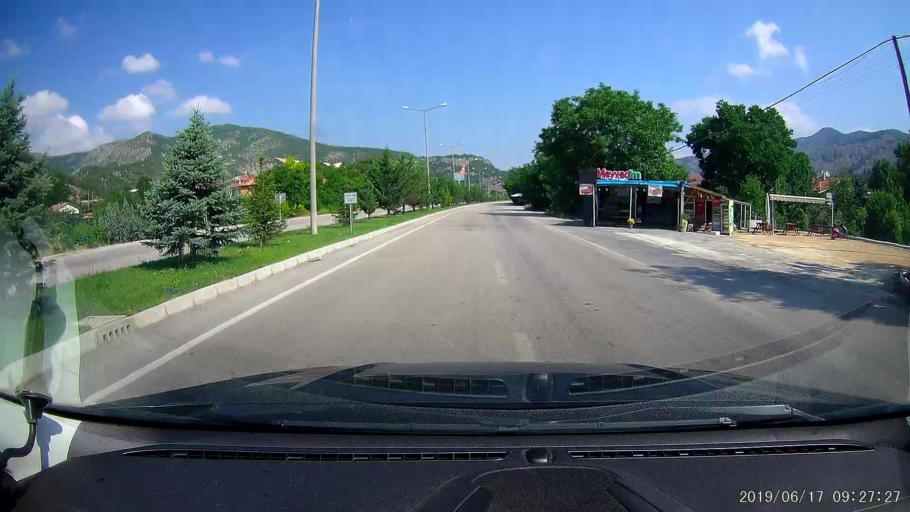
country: TR
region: Amasya
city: Amasya
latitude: 40.6773
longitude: 35.8264
